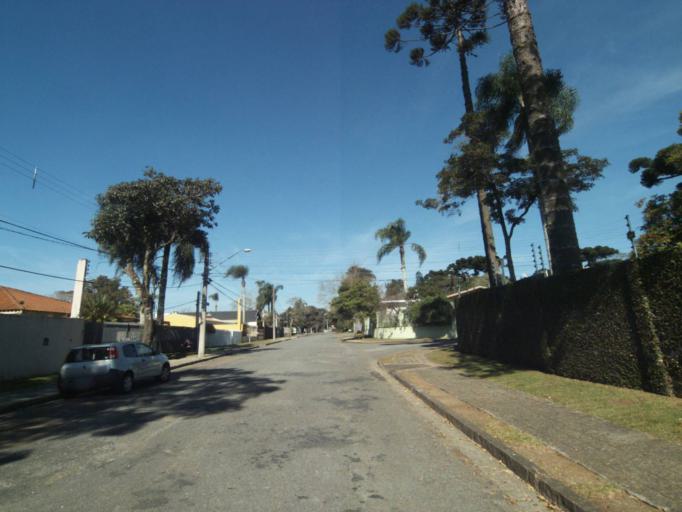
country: BR
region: Parana
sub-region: Curitiba
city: Curitiba
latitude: -25.4169
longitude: -49.2308
